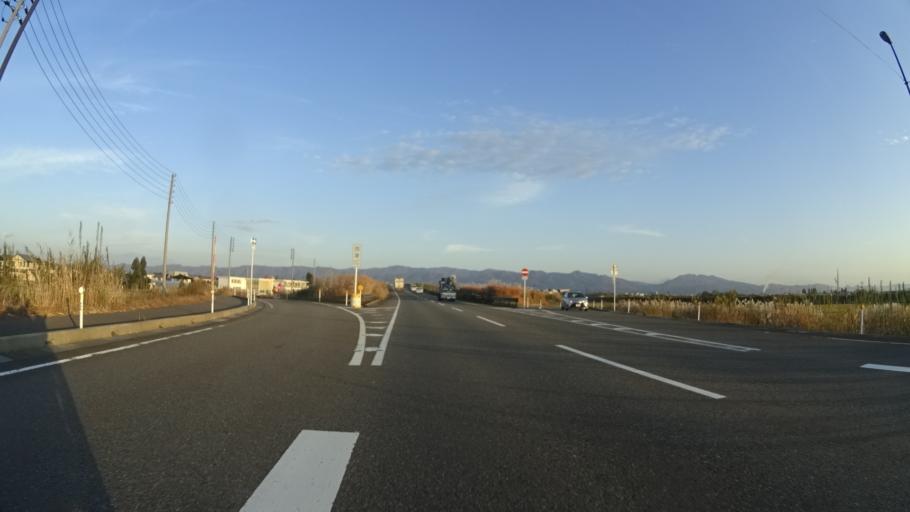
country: JP
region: Niigata
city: Nagaoka
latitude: 37.4344
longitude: 138.8075
